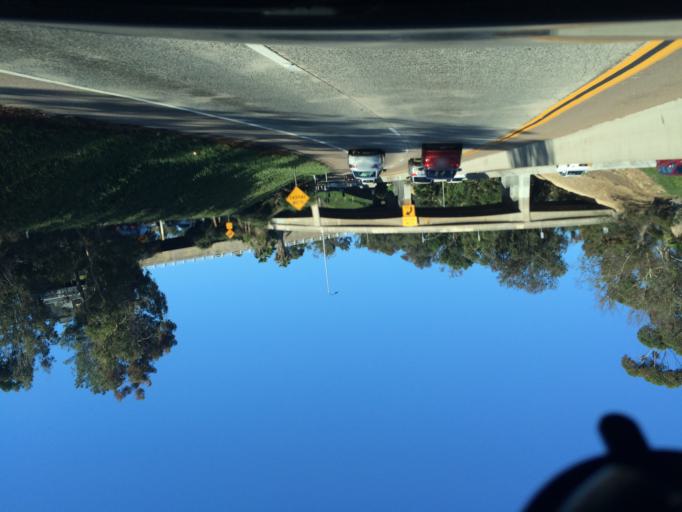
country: US
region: California
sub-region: San Diego County
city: San Diego
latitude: 32.7517
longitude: -117.1560
